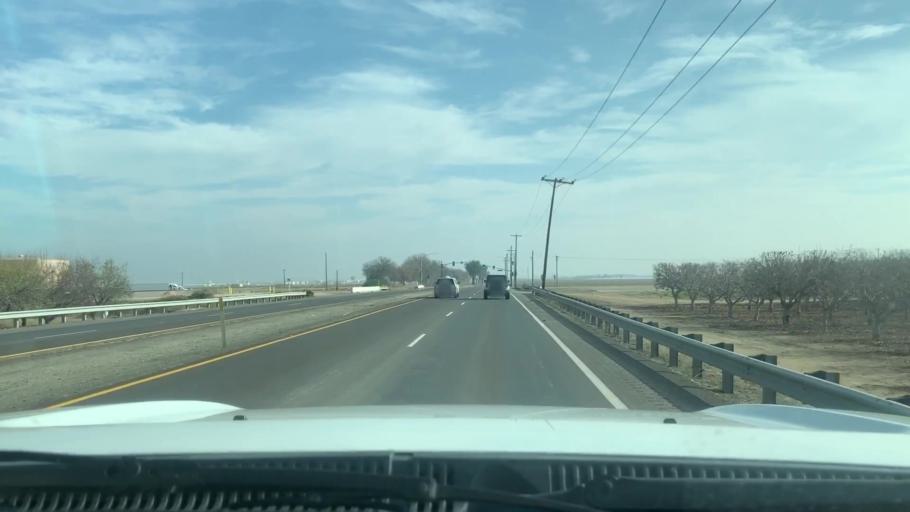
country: US
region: California
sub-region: Kern County
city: Shafter
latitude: 35.4997
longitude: -119.2085
